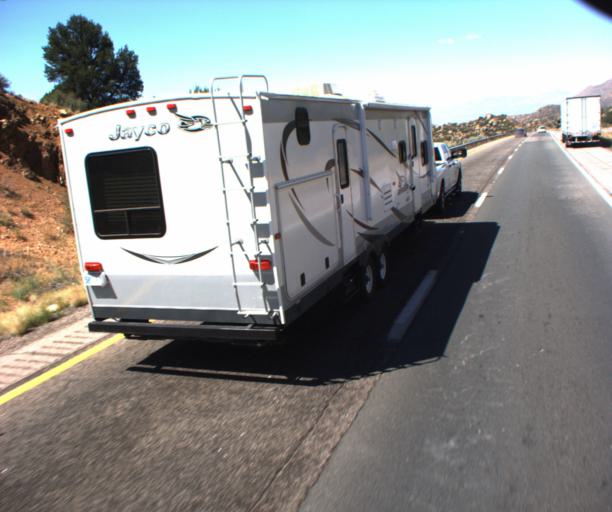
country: US
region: Arizona
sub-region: Mohave County
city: Peach Springs
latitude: 35.1801
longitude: -113.4786
